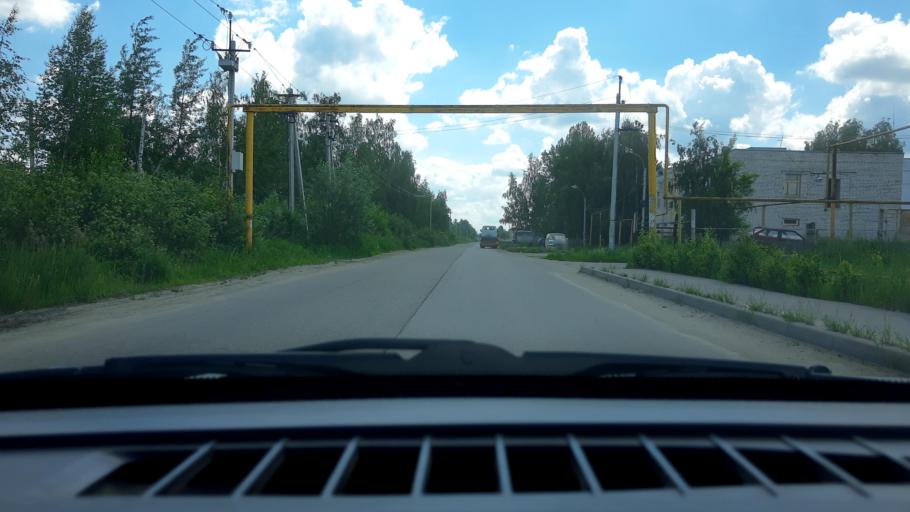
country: RU
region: Nizjnij Novgorod
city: Gorbatovka
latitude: 56.2545
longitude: 43.8080
